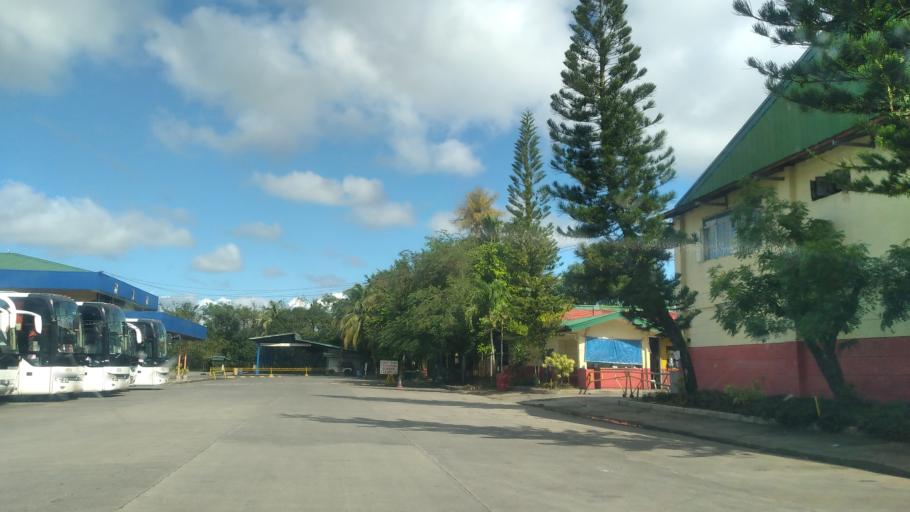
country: PH
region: Calabarzon
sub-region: Province of Quezon
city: Lucena
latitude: 13.9583
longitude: 121.6187
